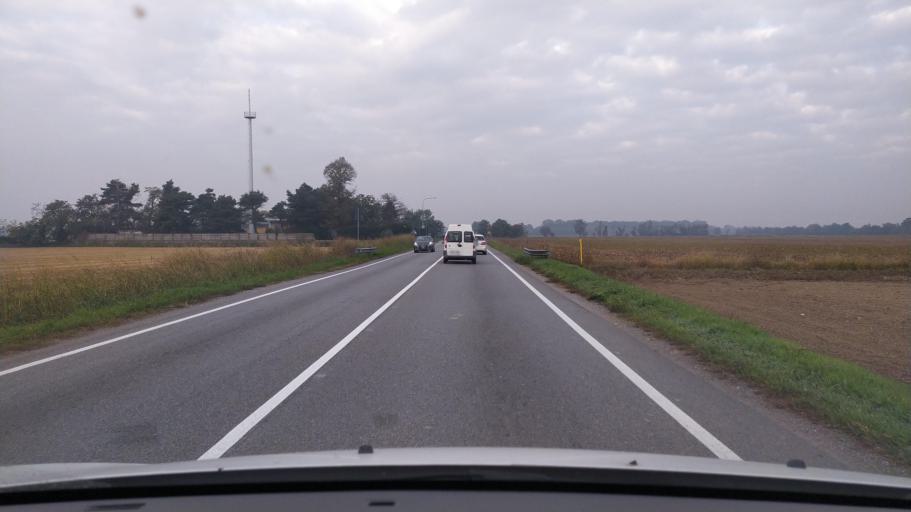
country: IT
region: Lombardy
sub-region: Citta metropolitana di Milano
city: Cusago
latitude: 45.4433
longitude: 9.0278
